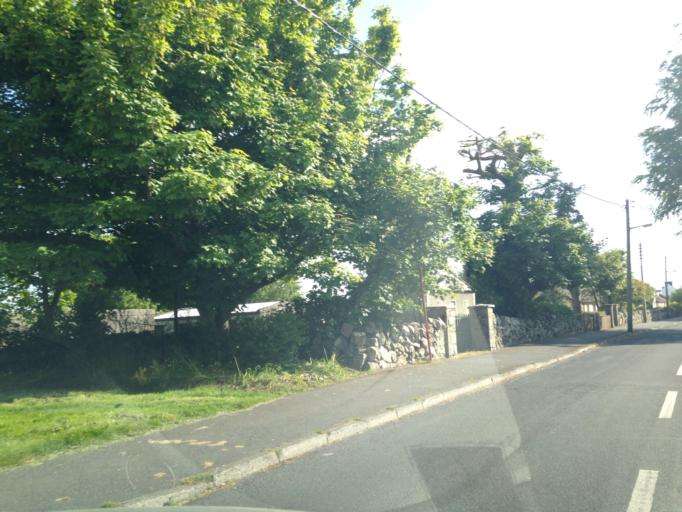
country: IE
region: Connaught
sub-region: County Galway
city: Gaillimh
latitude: 53.2770
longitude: -9.0237
